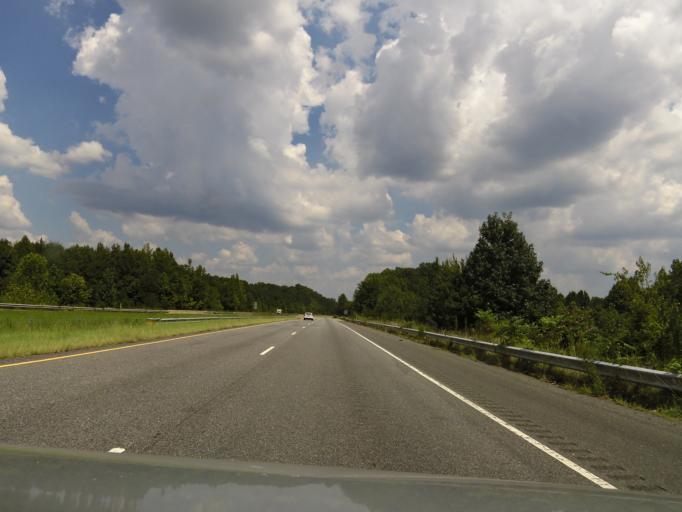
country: US
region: North Carolina
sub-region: Polk County
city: Columbus
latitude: 35.2862
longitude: -82.1042
